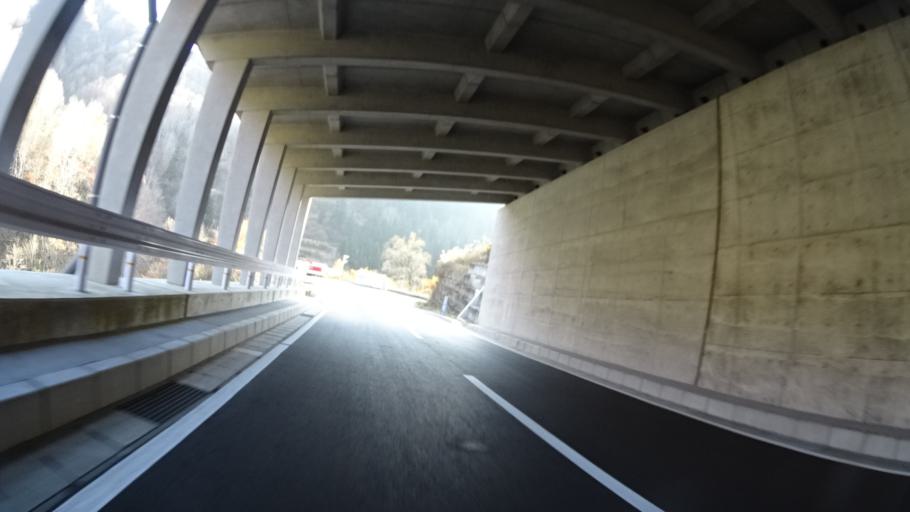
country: JP
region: Niigata
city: Shiozawa
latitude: 36.9854
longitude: 138.7596
